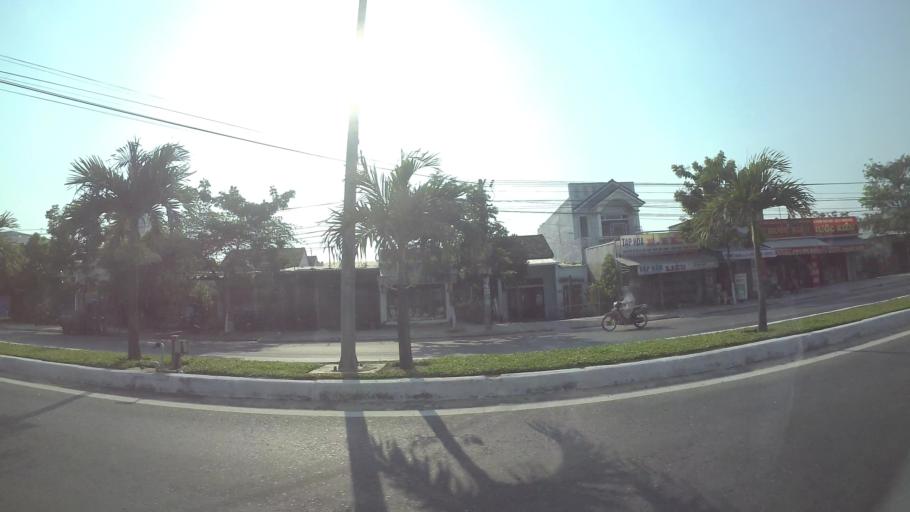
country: VN
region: Quang Nam
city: Quang Nam
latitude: 15.9471
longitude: 108.2546
